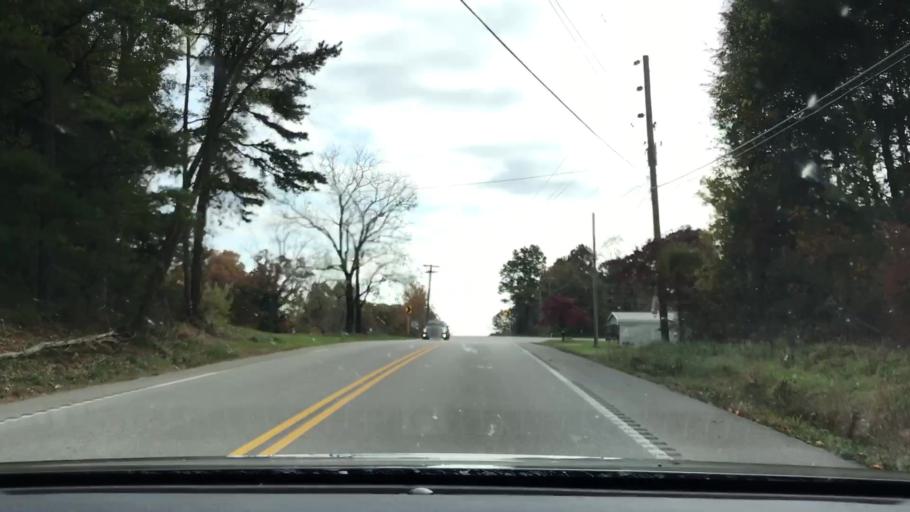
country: US
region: Tennessee
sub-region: Fentress County
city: Jamestown
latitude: 36.3803
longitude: -84.8779
